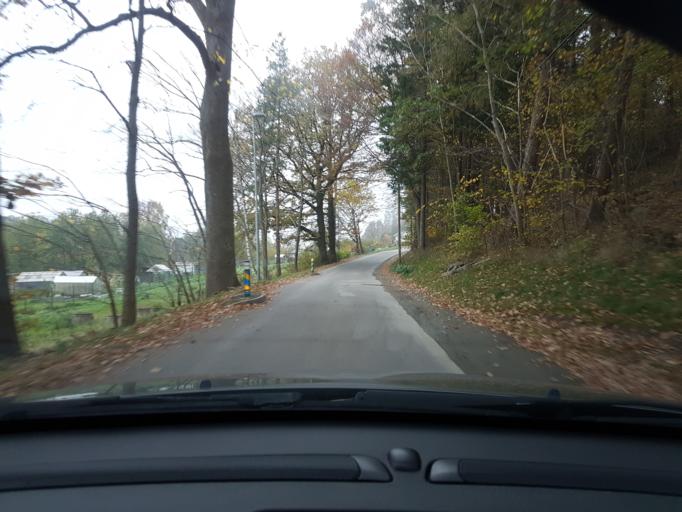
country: SE
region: Vaestra Goetaland
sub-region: Ale Kommun
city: Surte
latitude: 57.8211
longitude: 12.0230
